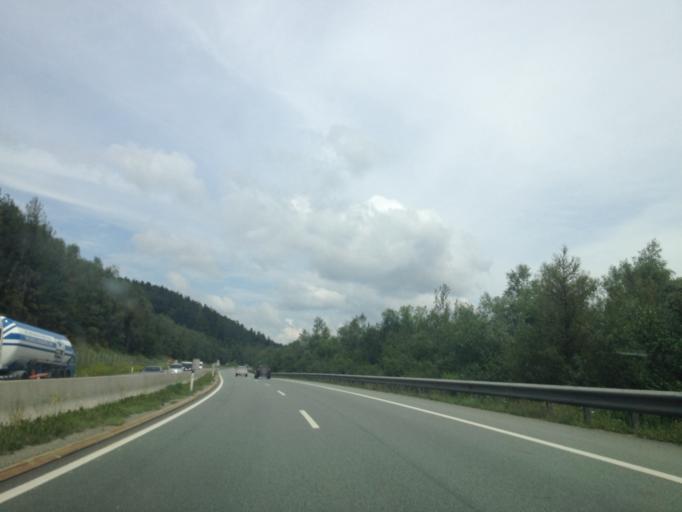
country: AT
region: Styria
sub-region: Politischer Bezirk Hartberg-Fuerstenfeld
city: Schaeffern
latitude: 47.4569
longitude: 16.0982
